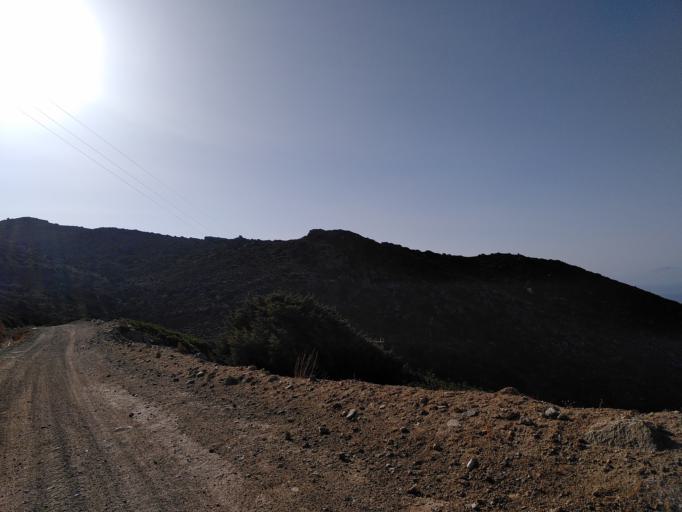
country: GR
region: South Aegean
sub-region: Nomos Kykladon
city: Ios
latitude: 36.7018
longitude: 25.3159
